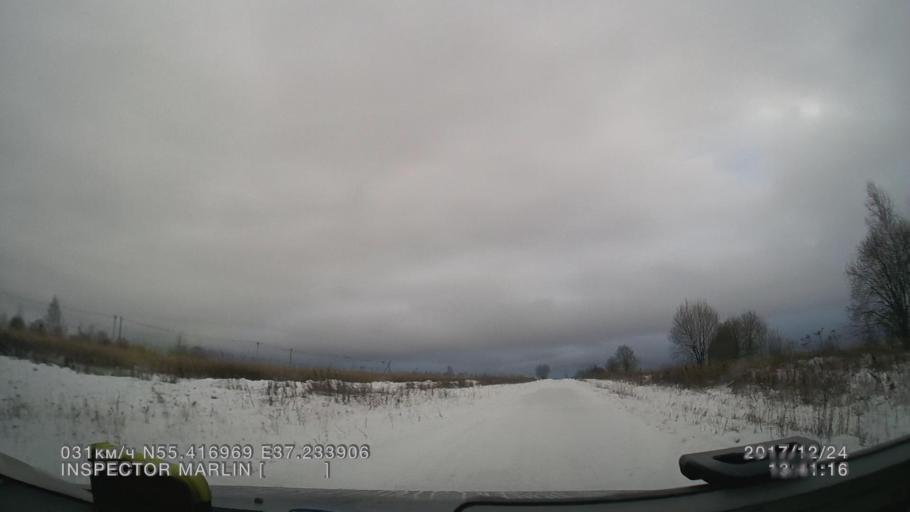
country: RU
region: Moskovskaya
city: Troitsk
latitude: 55.4170
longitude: 37.2339
